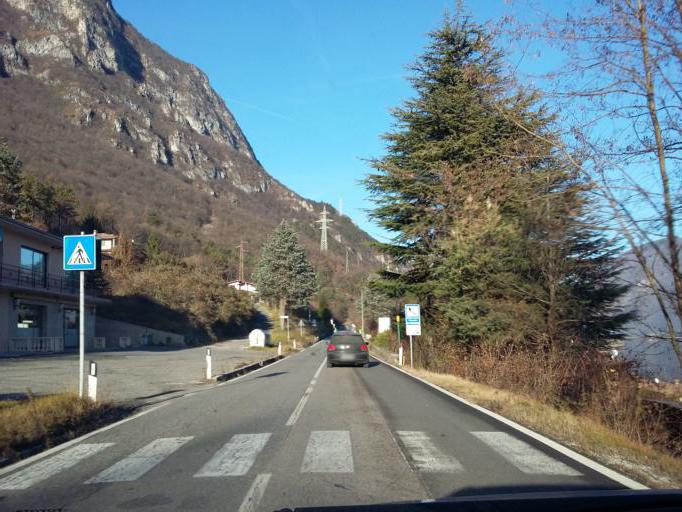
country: IT
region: Lombardy
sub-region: Provincia di Brescia
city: Crone
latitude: 45.7518
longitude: 10.4797
